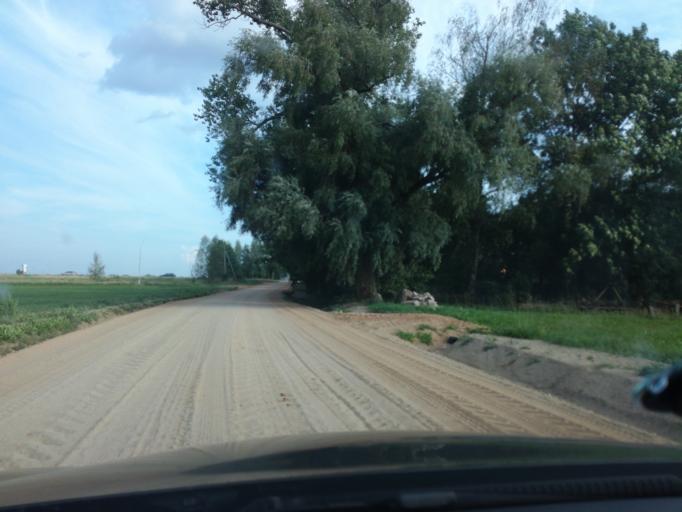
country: LT
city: Simnas
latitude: 54.3892
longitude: 23.8181
